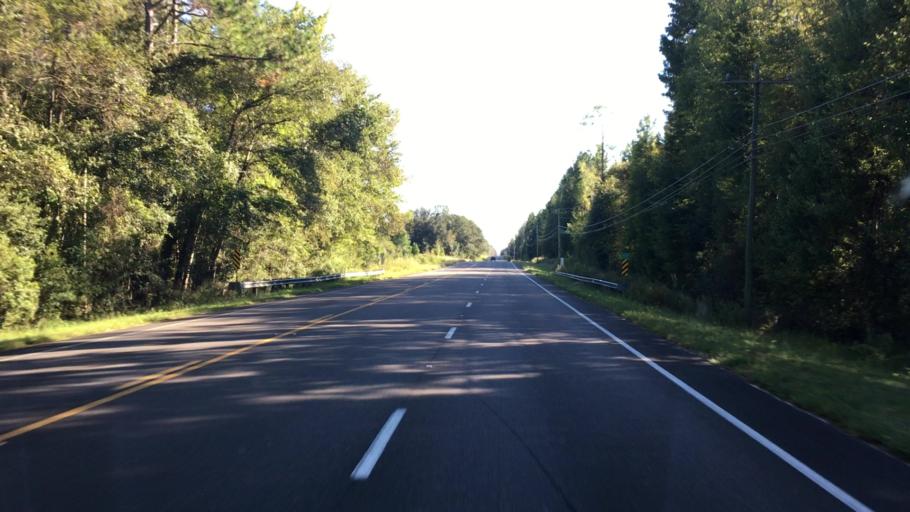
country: US
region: Florida
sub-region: Alachua County
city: Gainesville
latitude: 29.7348
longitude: -82.2767
